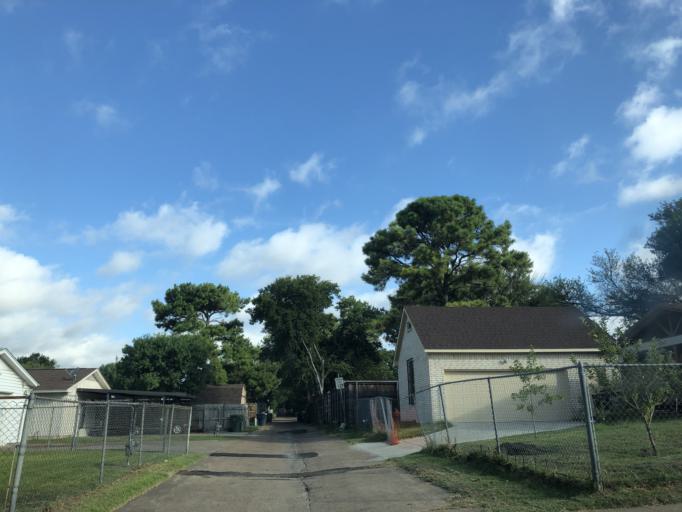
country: US
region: Texas
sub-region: Dallas County
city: Garland
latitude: 32.8502
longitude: -96.6392
